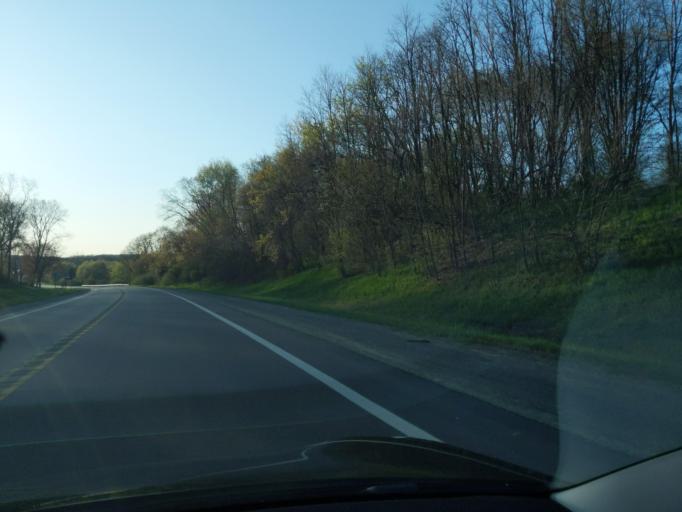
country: US
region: Michigan
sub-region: Washtenaw County
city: Chelsea
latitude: 42.3469
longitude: -84.0423
